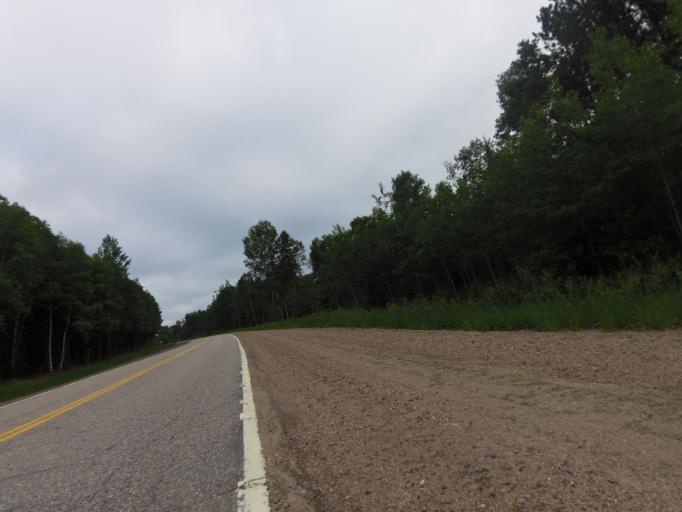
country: CA
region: Quebec
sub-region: Outaouais
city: Shawville
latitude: 45.9110
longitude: -76.3145
